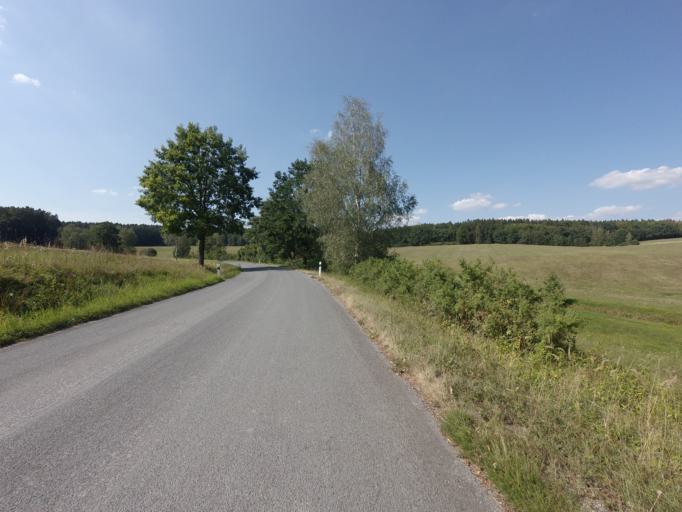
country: CZ
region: Jihocesky
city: Tyn nad Vltavou
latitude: 49.1542
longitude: 14.4413
